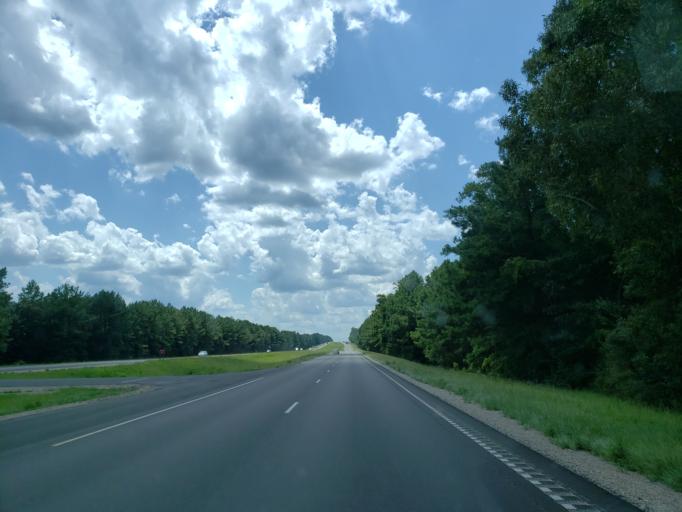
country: US
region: Mississippi
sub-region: Perry County
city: New Augusta
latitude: 31.2112
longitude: -89.1344
